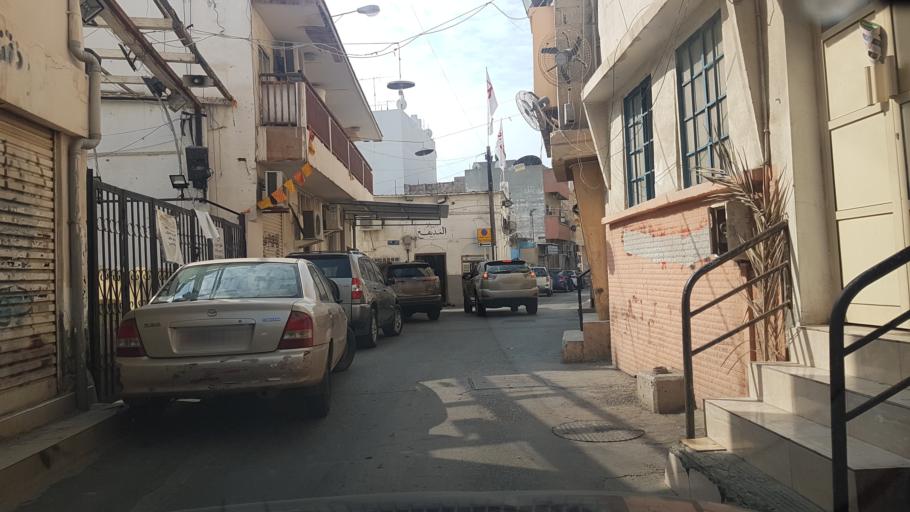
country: BH
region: Manama
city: Manama
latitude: 26.2297
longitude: 50.5788
